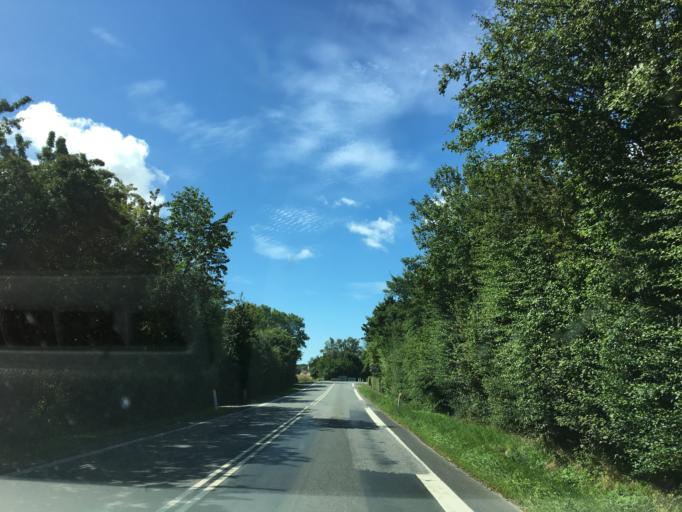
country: DK
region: South Denmark
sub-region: Langeland Kommune
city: Rudkobing
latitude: 54.8433
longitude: 10.7114
